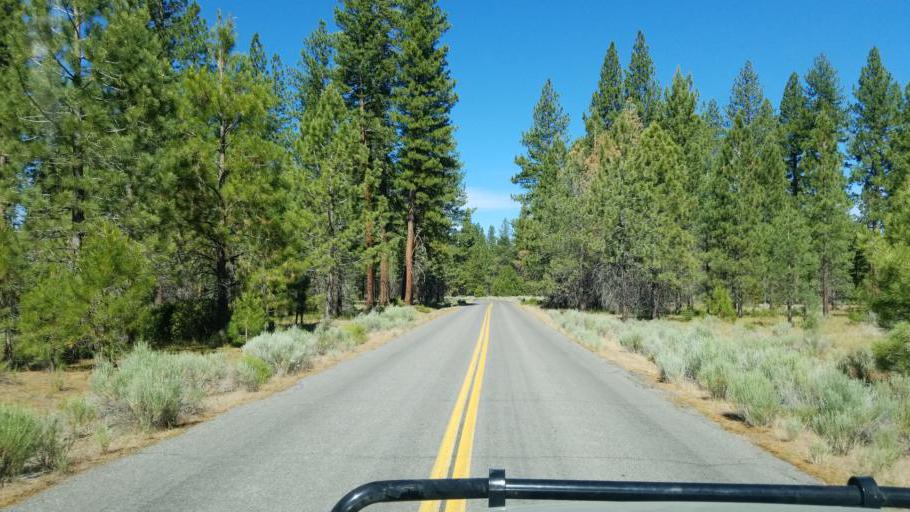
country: US
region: California
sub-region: Lassen County
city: Susanville
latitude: 40.5477
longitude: -120.7816
